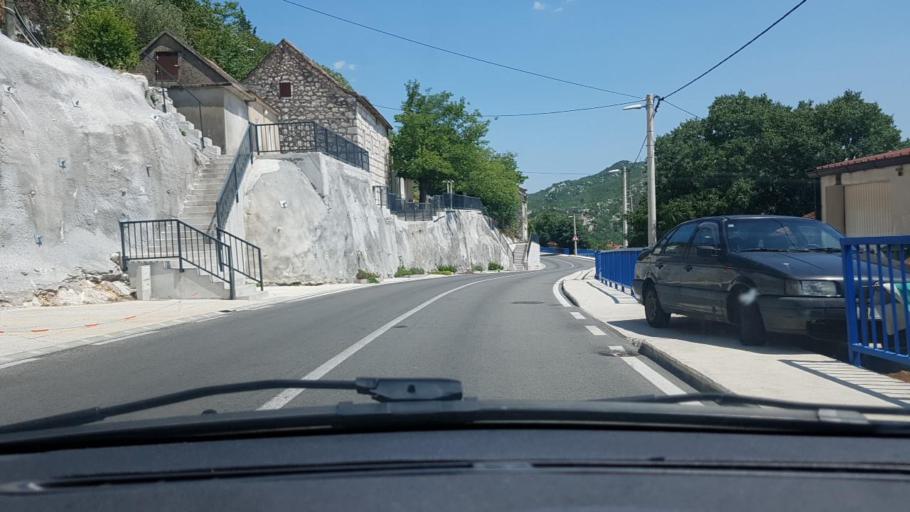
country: HR
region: Splitsko-Dalmatinska
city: Vrgorac
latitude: 43.2050
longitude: 17.3643
